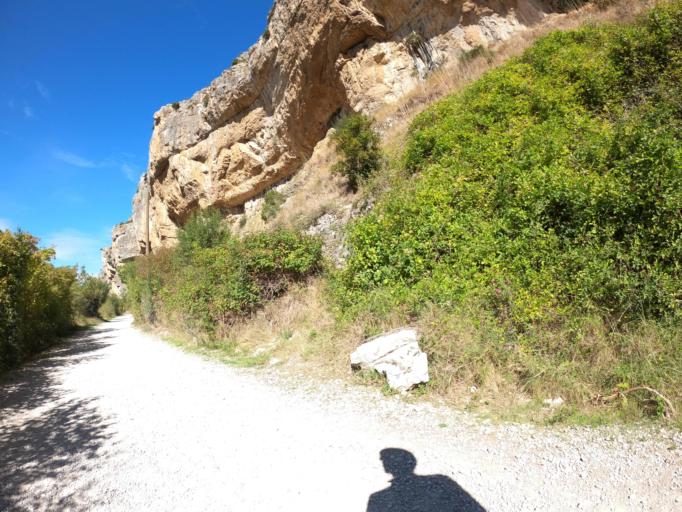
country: ES
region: Navarre
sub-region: Provincia de Navarra
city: Lumbier
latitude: 42.6326
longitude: -1.3015
